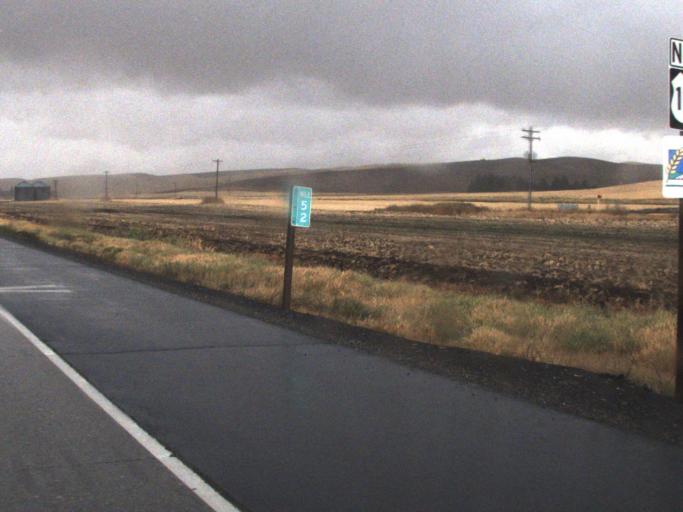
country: US
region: Washington
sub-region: Whitman County
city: Colfax
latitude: 47.0596
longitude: -117.3813
